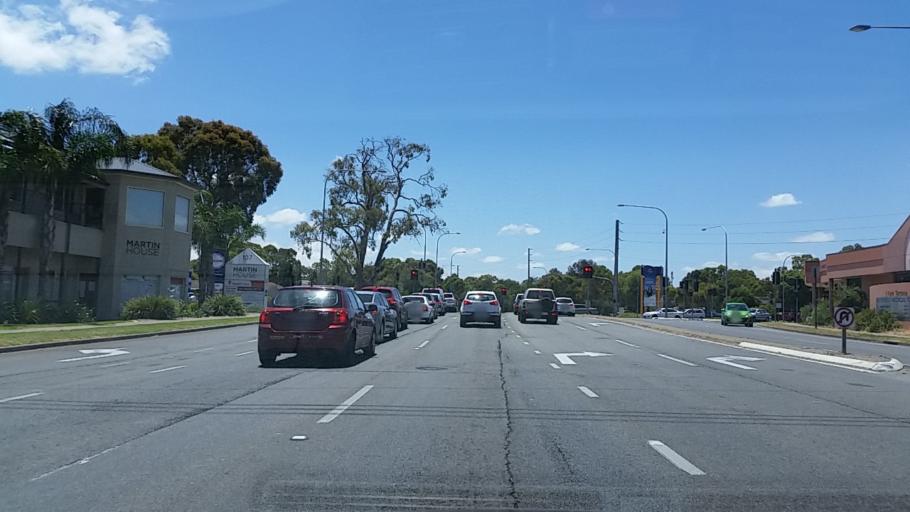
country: AU
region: South Australia
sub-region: Salisbury
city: Salisbury
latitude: -34.7642
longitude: 138.6397
